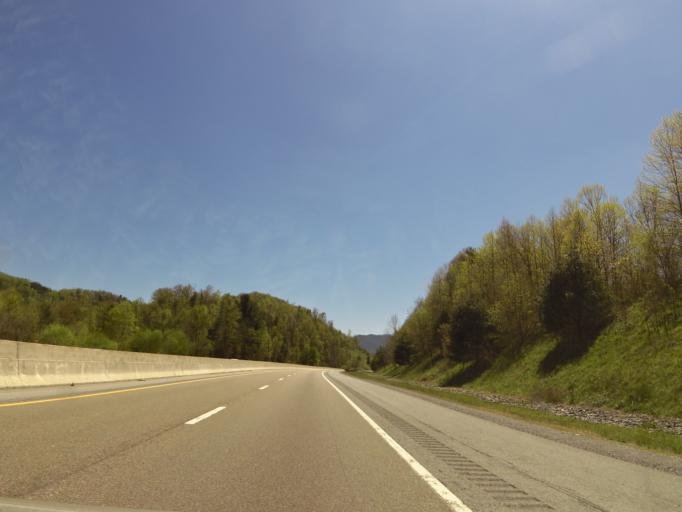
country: US
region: Tennessee
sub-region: Unicoi County
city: Banner Hill
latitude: 36.0299
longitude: -82.5410
